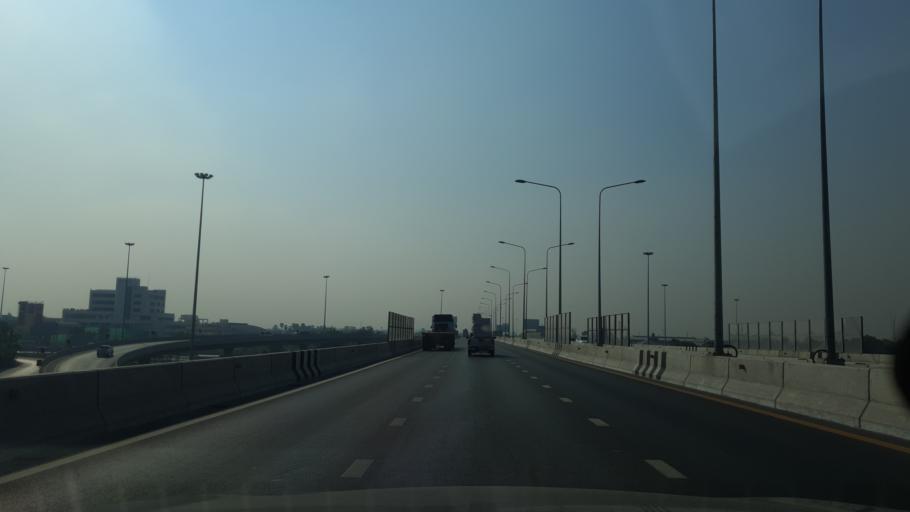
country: TH
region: Nonthaburi
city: Bang Bua Thong
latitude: 13.9530
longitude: 100.4586
